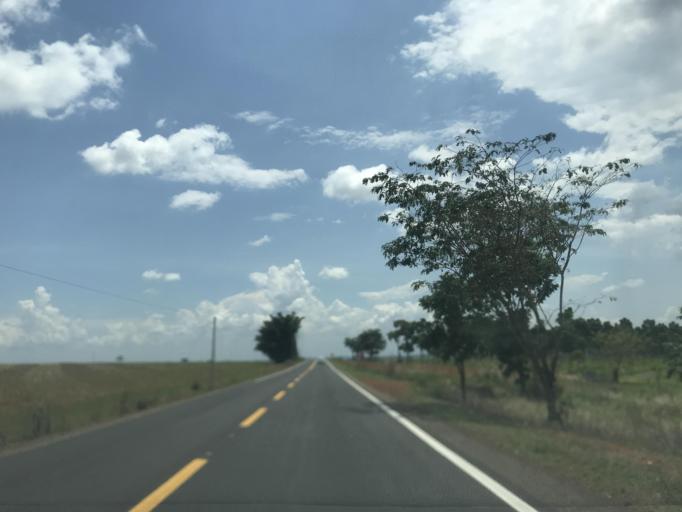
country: BR
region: Goias
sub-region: Bela Vista De Goias
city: Bela Vista de Goias
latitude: -17.0974
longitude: -48.6580
